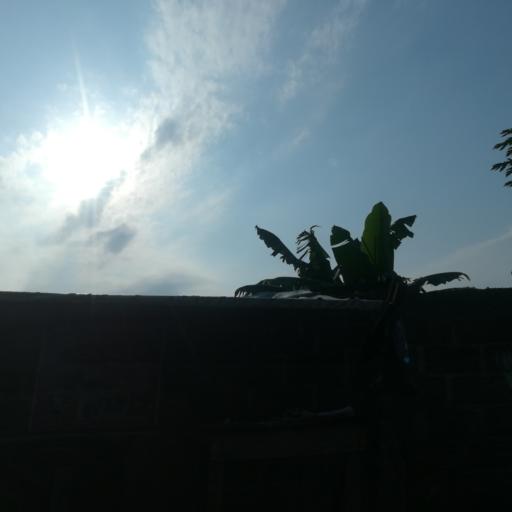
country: NG
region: Rivers
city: Port Harcourt
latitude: 4.8565
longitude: 6.9648
